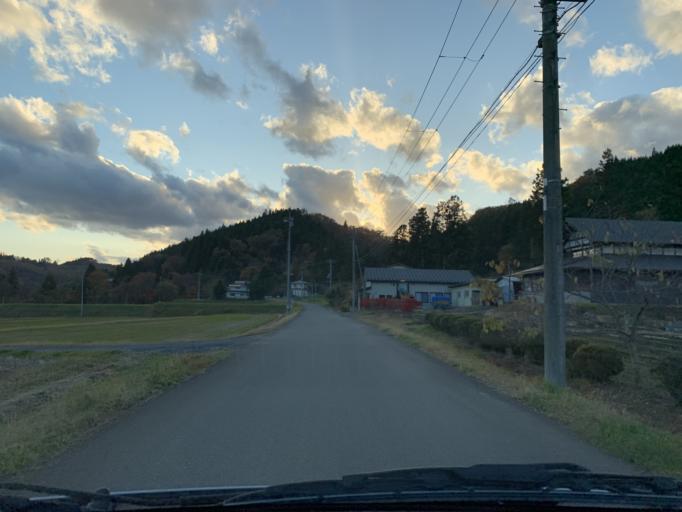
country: JP
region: Iwate
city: Mizusawa
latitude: 39.0316
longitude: 141.0402
